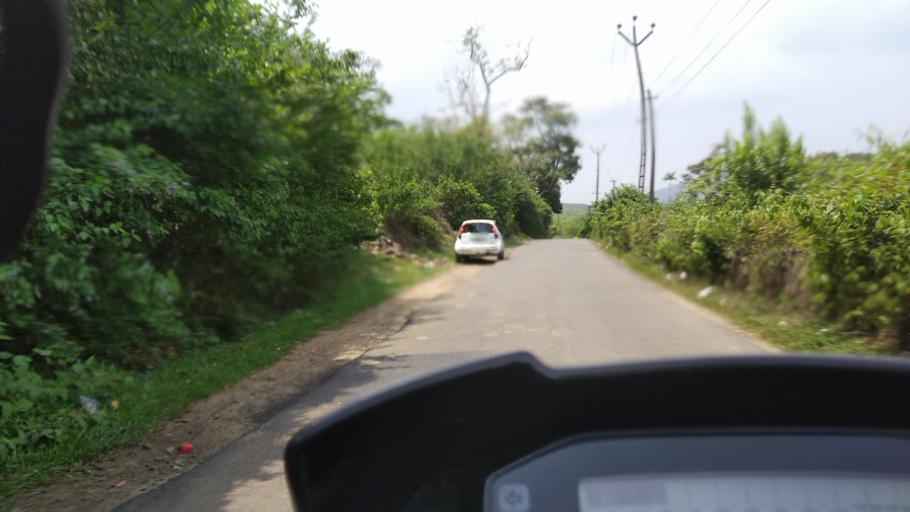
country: IN
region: Kerala
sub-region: Kottayam
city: Erattupetta
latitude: 9.6392
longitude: 76.9302
